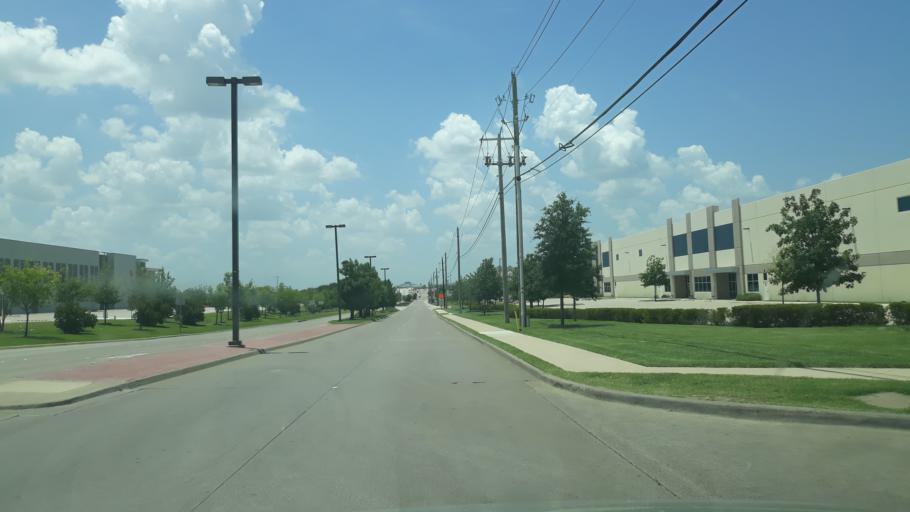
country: US
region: Texas
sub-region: Dallas County
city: Coppell
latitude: 32.9553
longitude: -97.0299
